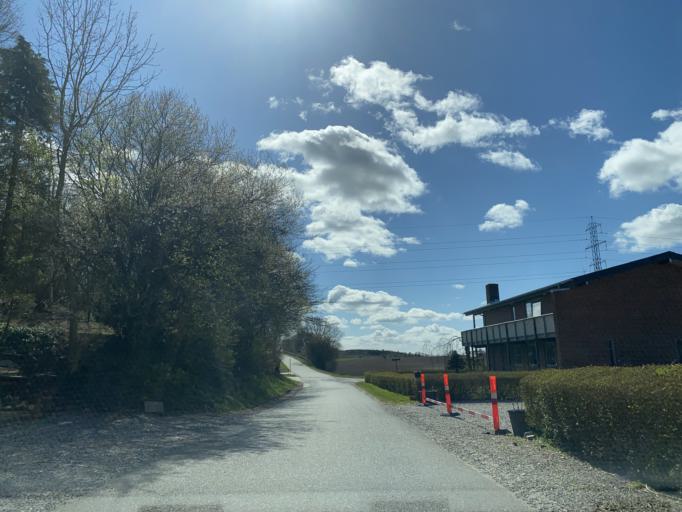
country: DK
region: Central Jutland
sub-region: Favrskov Kommune
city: Ulstrup
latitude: 56.3411
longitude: 9.7884
